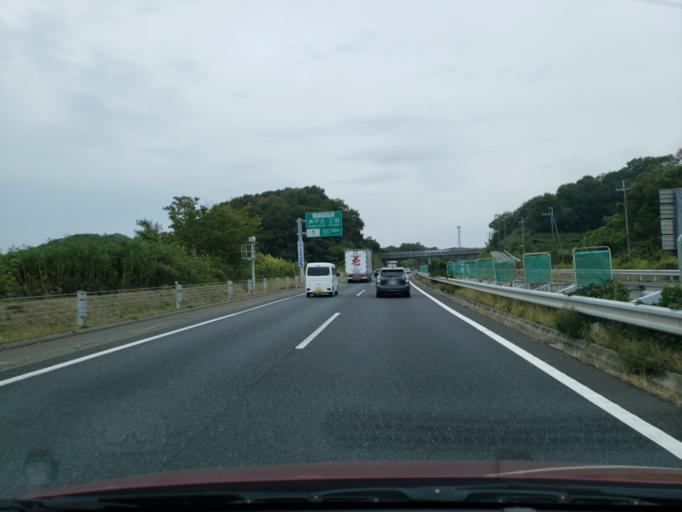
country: JP
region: Hyogo
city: Sandacho
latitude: 34.8339
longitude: 135.1879
